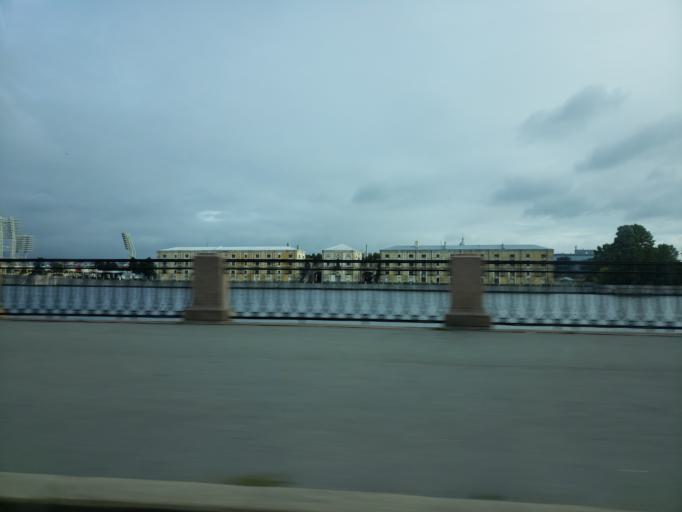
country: RU
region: St.-Petersburg
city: Saint Petersburg
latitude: 59.9466
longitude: 30.2889
